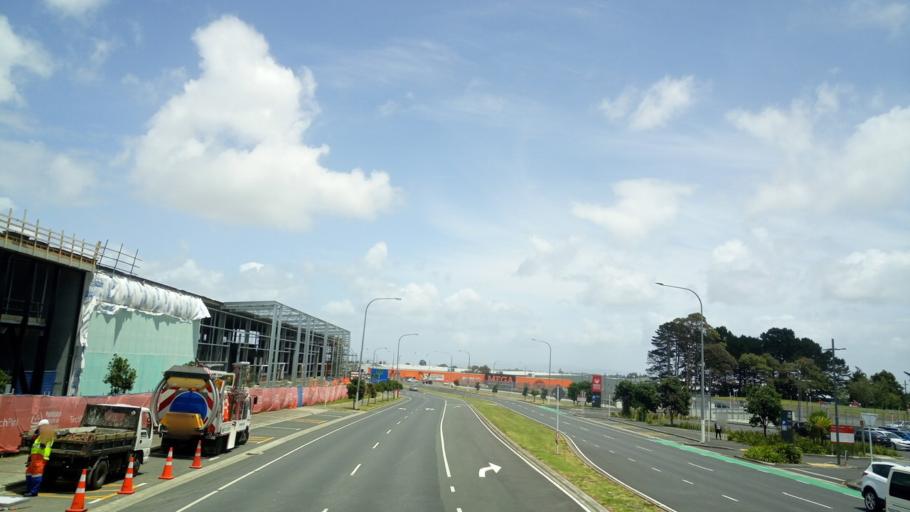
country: NZ
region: Auckland
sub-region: Auckland
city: Manukau City
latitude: -36.9946
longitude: 174.8773
